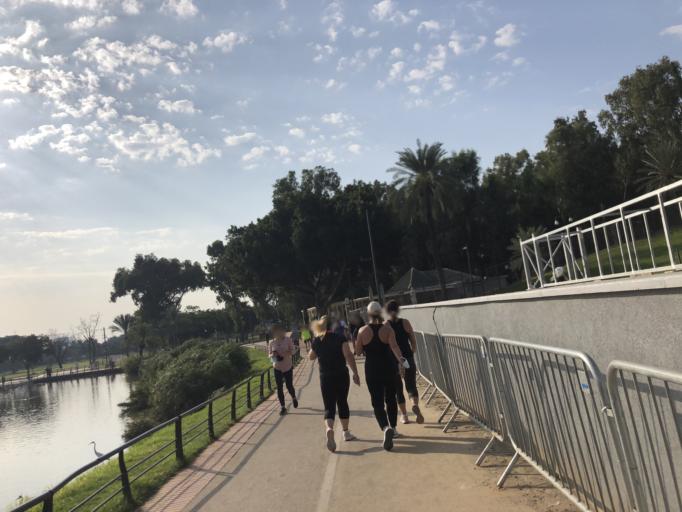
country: IL
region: Tel Aviv
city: Giv`atayim
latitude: 32.0500
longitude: 34.8232
